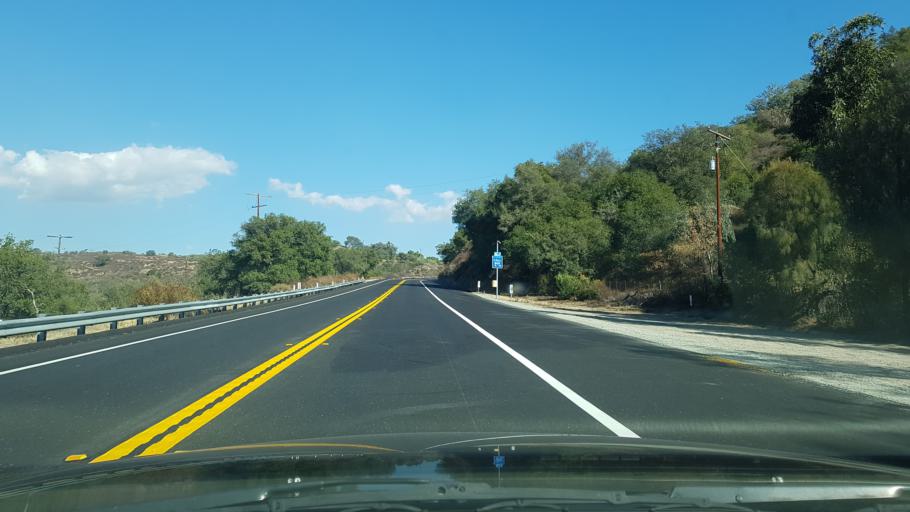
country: US
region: California
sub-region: San Diego County
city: San Diego Country Estates
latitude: 33.0672
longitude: -116.7328
